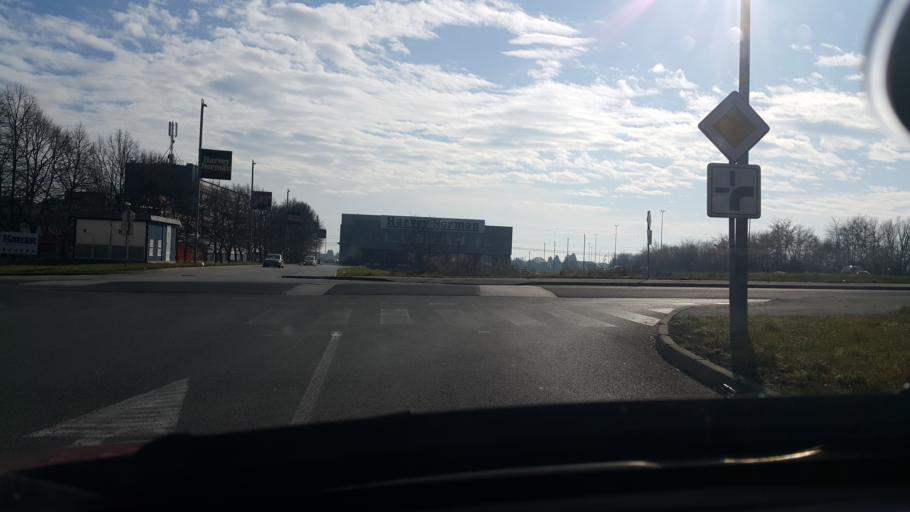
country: SI
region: Maribor
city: Razvanje
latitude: 46.5174
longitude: 15.6521
